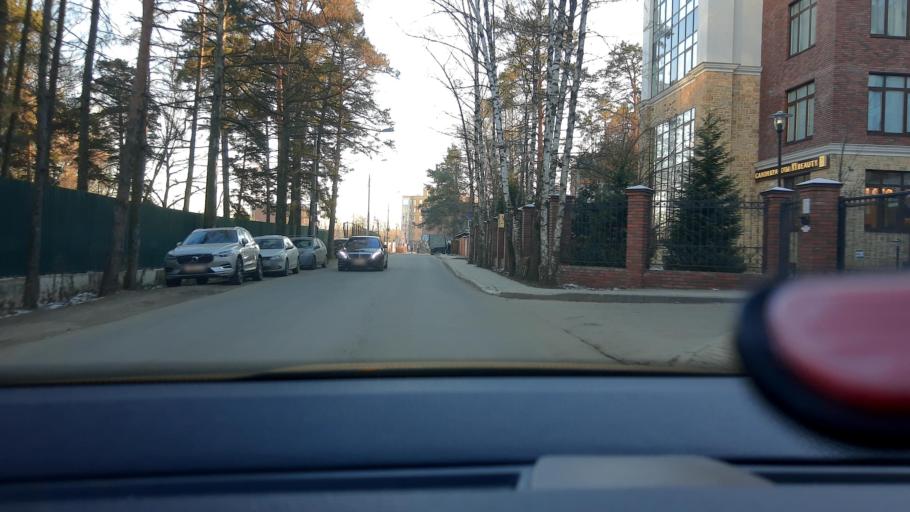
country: RU
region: Moskovskaya
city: Zarech'ye
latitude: 55.6812
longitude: 37.3856
